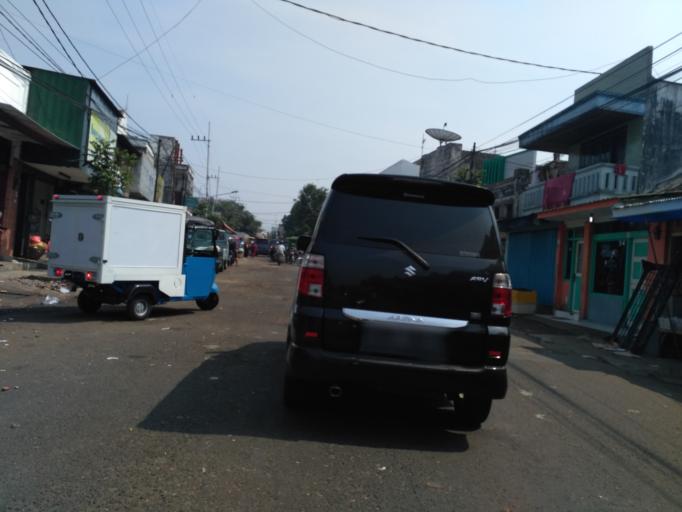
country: ID
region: East Java
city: Malang
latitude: -7.9882
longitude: 112.6381
